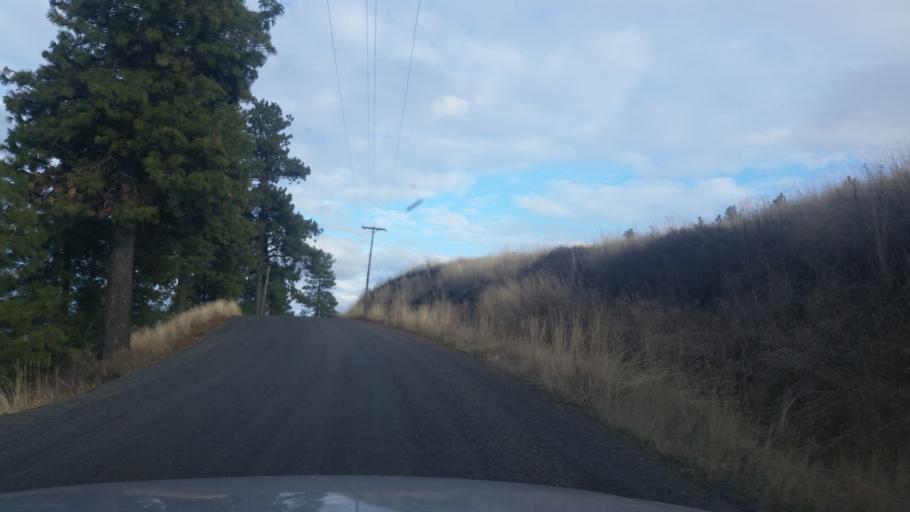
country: US
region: Washington
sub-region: Spokane County
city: Cheney
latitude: 47.4273
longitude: -117.4250
